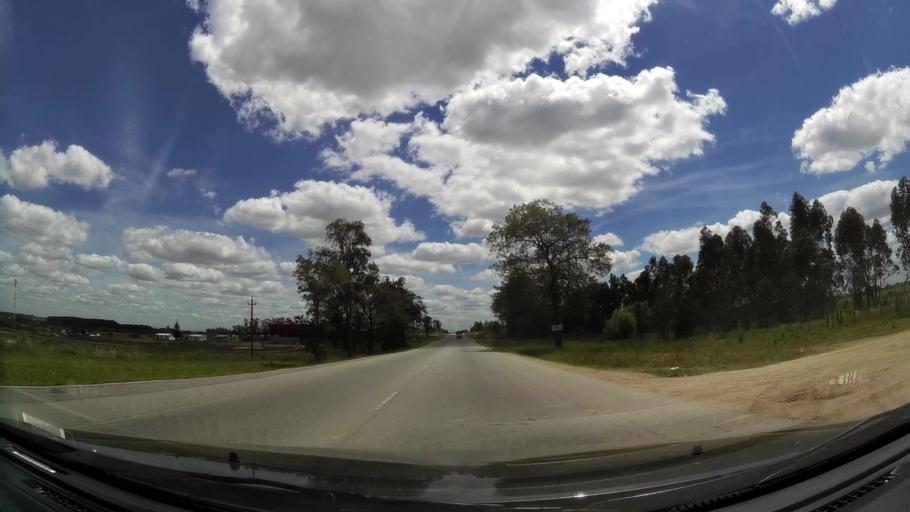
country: UY
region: Canelones
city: Colonia Nicolich
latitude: -34.8092
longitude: -56.0061
